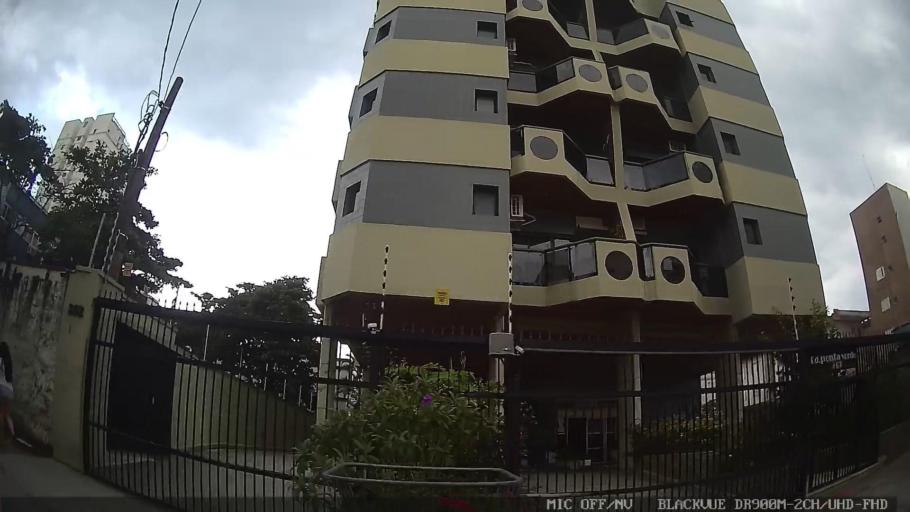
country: BR
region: Sao Paulo
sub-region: Guaruja
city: Guaruja
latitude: -23.9844
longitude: -46.2343
